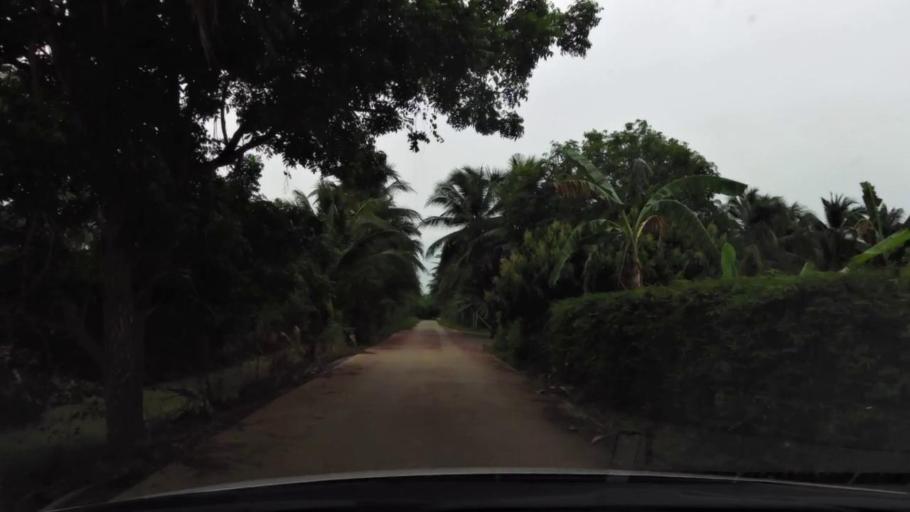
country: TH
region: Samut Sakhon
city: Ban Phaeo
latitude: 13.5917
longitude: 100.0346
